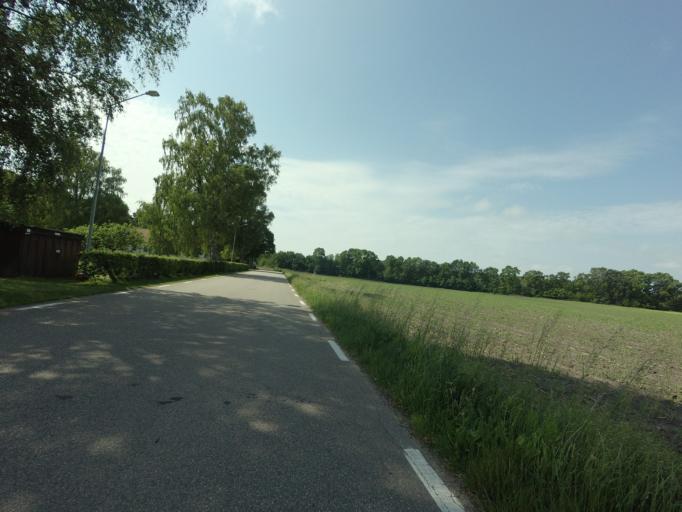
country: SE
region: Skane
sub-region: Helsingborg
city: Odakra
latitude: 56.2143
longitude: 12.7105
